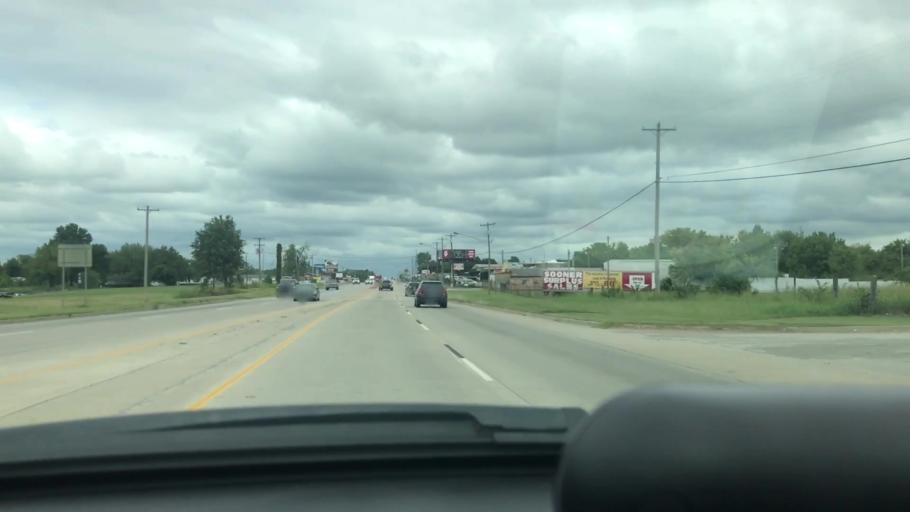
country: US
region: Oklahoma
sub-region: Muskogee County
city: Muskogee
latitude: 35.7715
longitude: -95.4025
